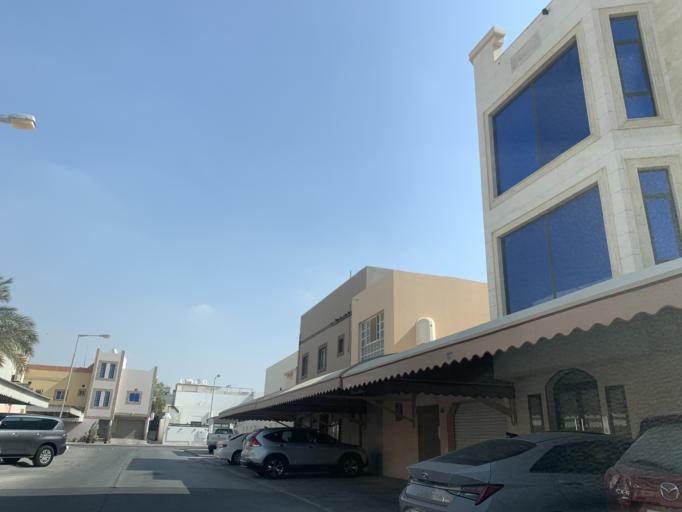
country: BH
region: Central Governorate
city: Madinat Hamad
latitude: 26.1263
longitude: 50.4924
